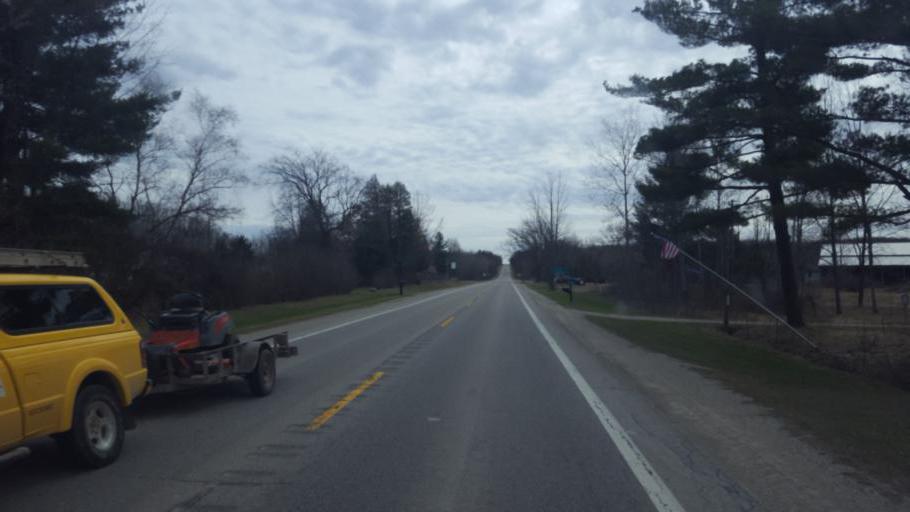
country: US
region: Michigan
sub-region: Isabella County
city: Lake Isabella
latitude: 43.6925
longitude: -85.1466
